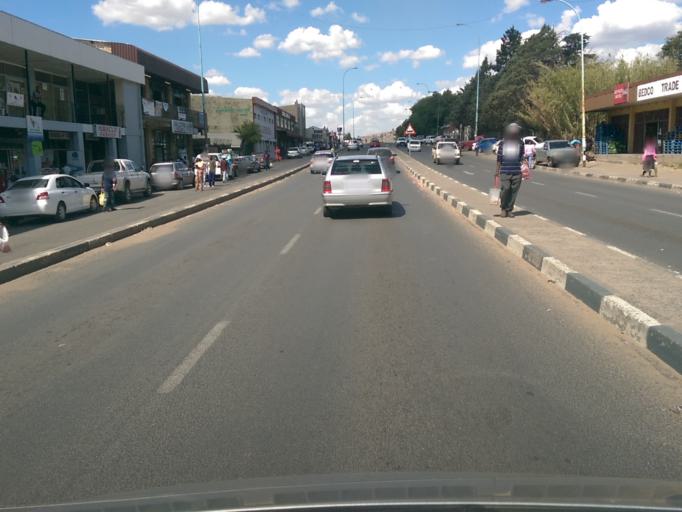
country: LS
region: Maseru
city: Maseru
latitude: -29.3156
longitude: 27.4976
